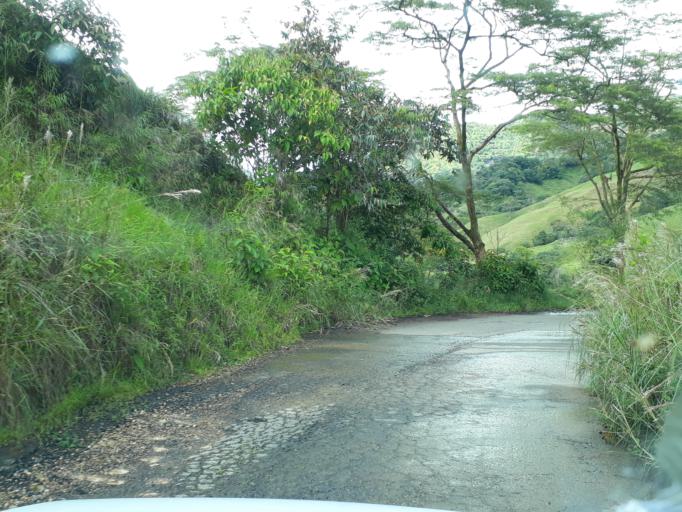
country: CO
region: Cundinamarca
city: Medina
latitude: 4.6327
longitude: -73.3120
